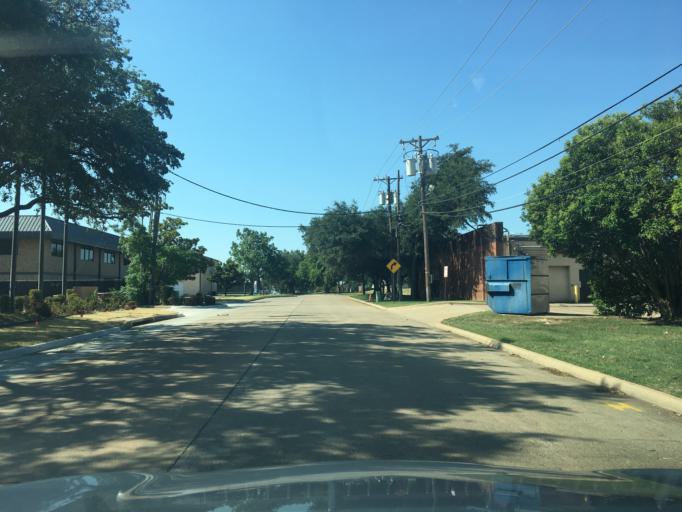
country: US
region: Texas
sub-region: Dallas County
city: Addison
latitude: 32.9676
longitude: -96.8385
